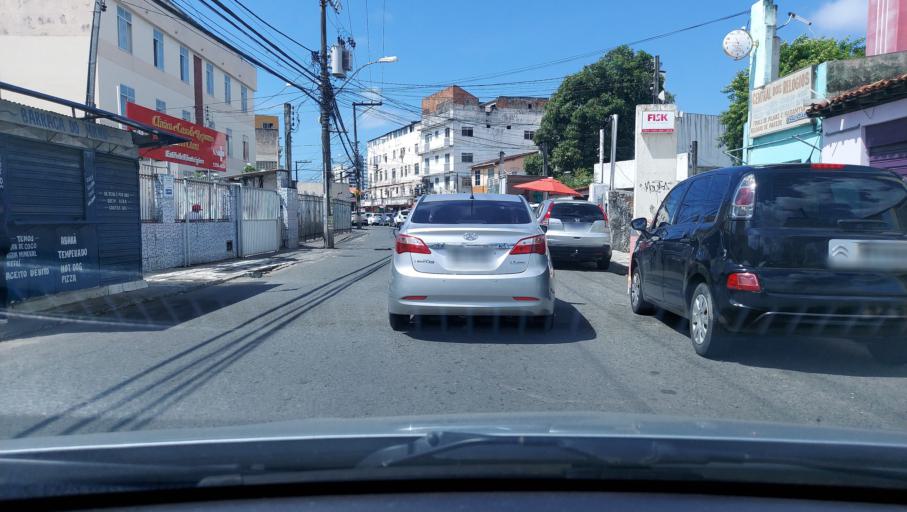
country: BR
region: Bahia
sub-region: Salvador
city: Salvador
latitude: -12.9871
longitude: -38.4788
